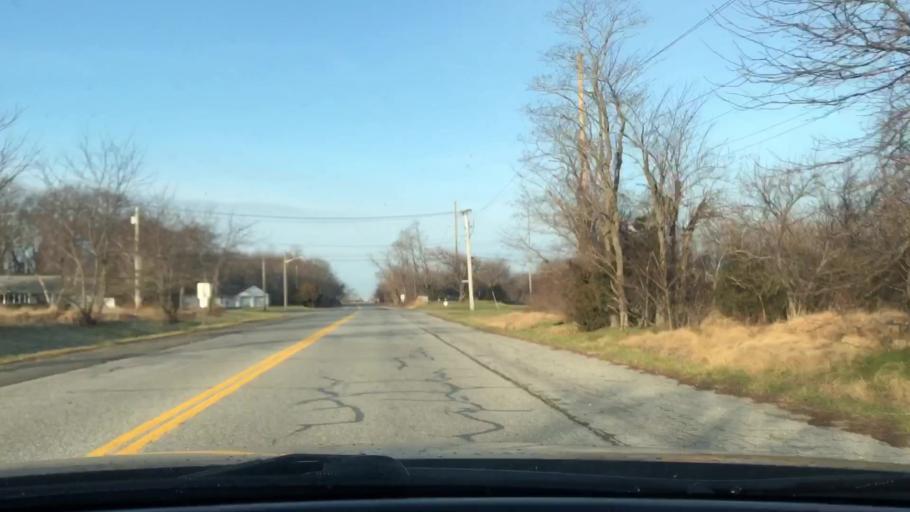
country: US
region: New York
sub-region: Suffolk County
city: Calverton
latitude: 40.9293
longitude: -72.7274
